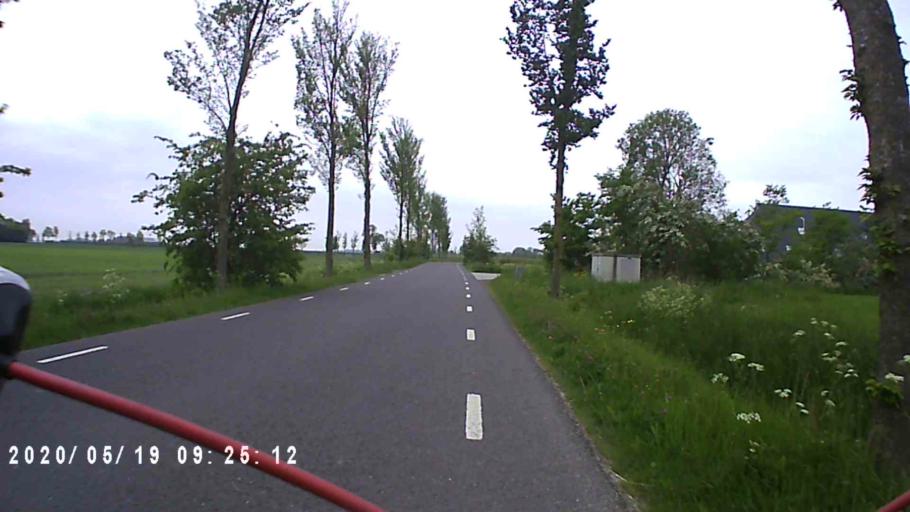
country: NL
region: Groningen
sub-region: Gemeente Zuidhorn
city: Grijpskerk
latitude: 53.2922
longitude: 6.3355
